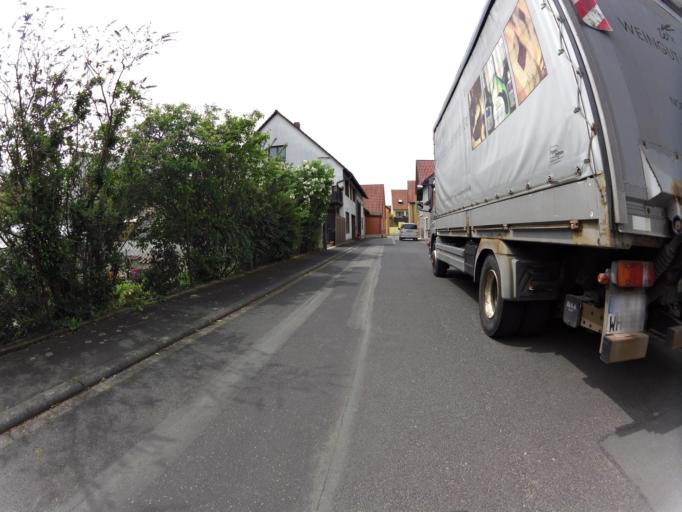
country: DE
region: Bavaria
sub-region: Regierungsbezirk Unterfranken
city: Nordheim
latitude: 49.8603
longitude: 10.1864
